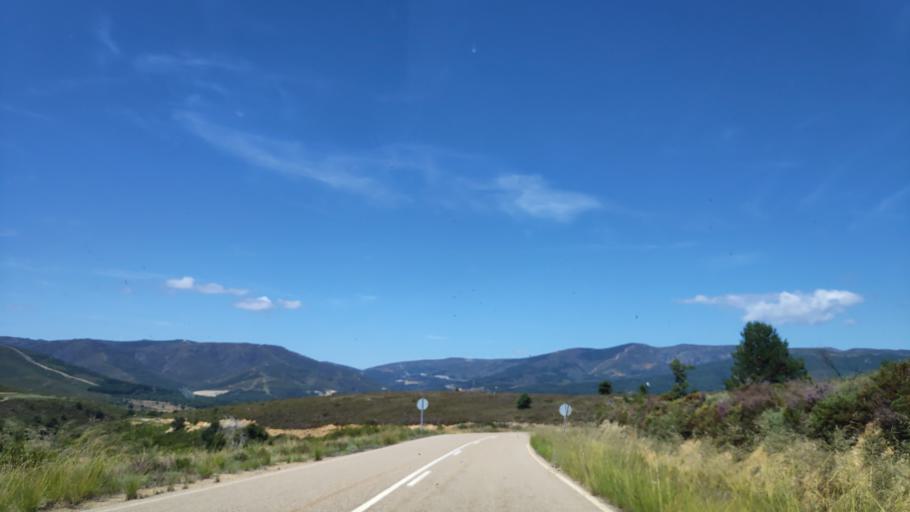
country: ES
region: Castille and Leon
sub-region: Provincia de Zamora
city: Requejo
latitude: 42.0201
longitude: -6.6920
